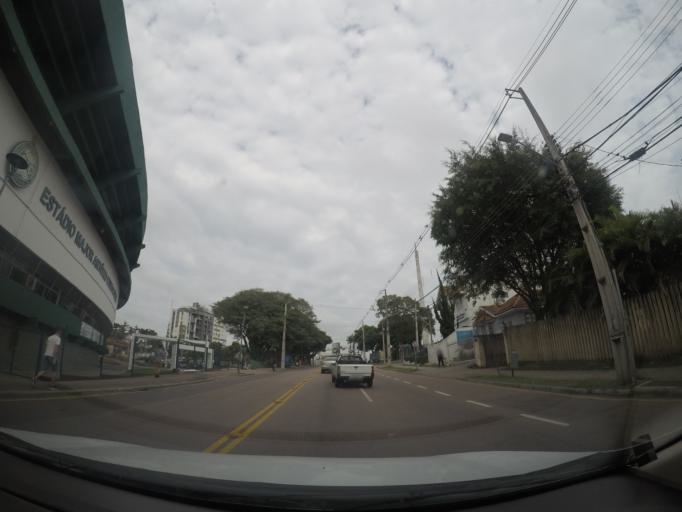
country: BR
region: Parana
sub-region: Curitiba
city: Curitiba
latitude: -25.4205
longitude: -49.2606
